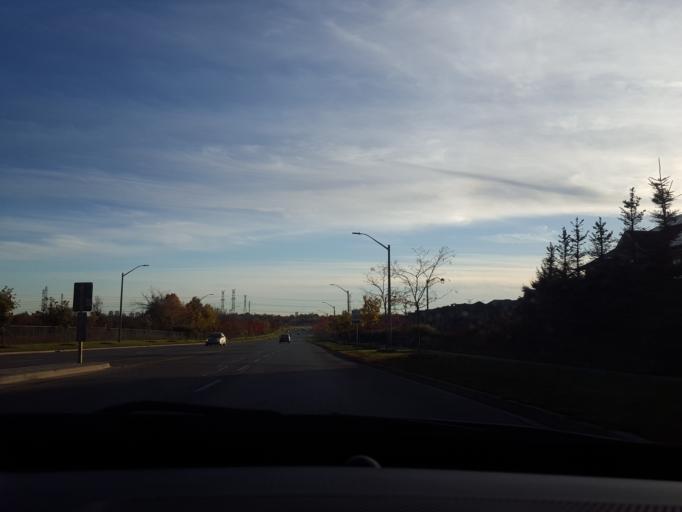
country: CA
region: Ontario
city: Markham
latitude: 43.8570
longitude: -79.2200
